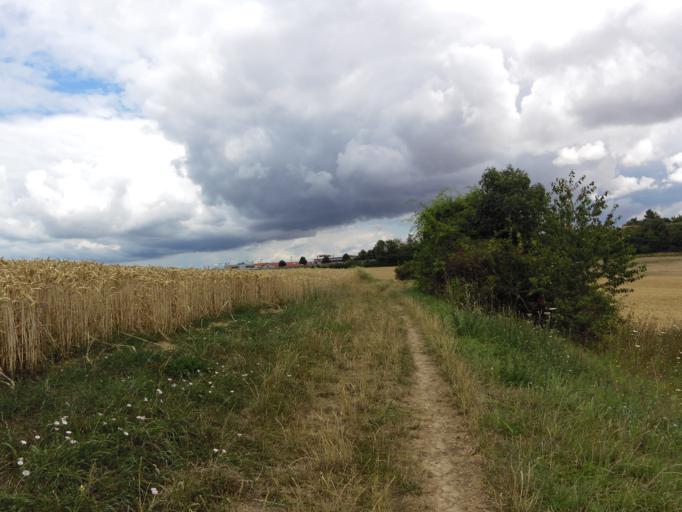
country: DE
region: Bavaria
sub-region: Regierungsbezirk Unterfranken
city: Wuerzburg
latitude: 49.8159
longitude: 9.9749
